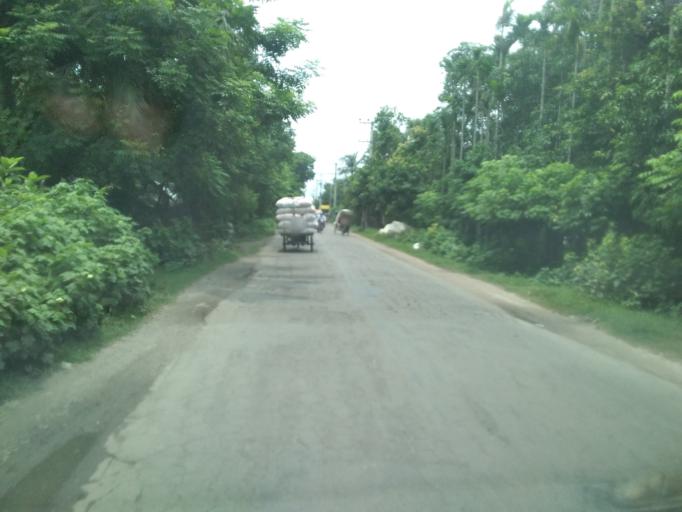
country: IN
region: West Bengal
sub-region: North 24 Parganas
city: Taki
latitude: 22.5731
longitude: 89.0001
